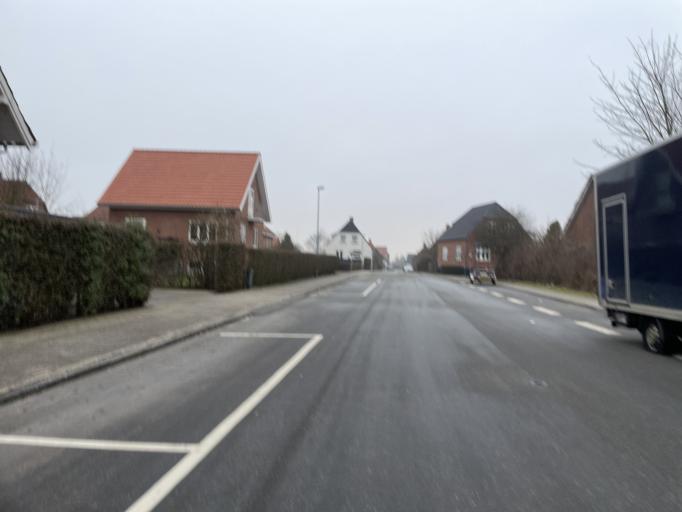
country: DK
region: South Denmark
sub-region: Fredericia Kommune
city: Fredericia
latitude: 55.5739
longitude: 9.7585
